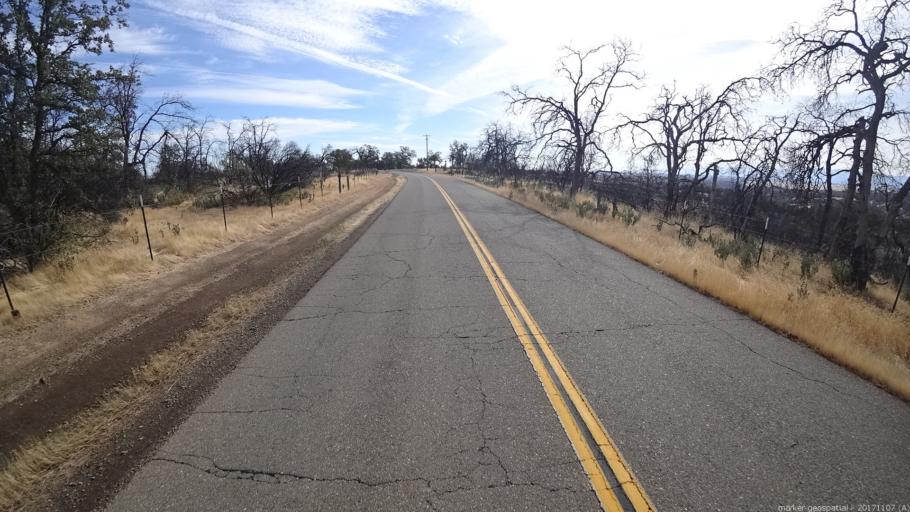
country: US
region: California
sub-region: Shasta County
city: Shasta
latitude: 40.4707
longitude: -122.5444
